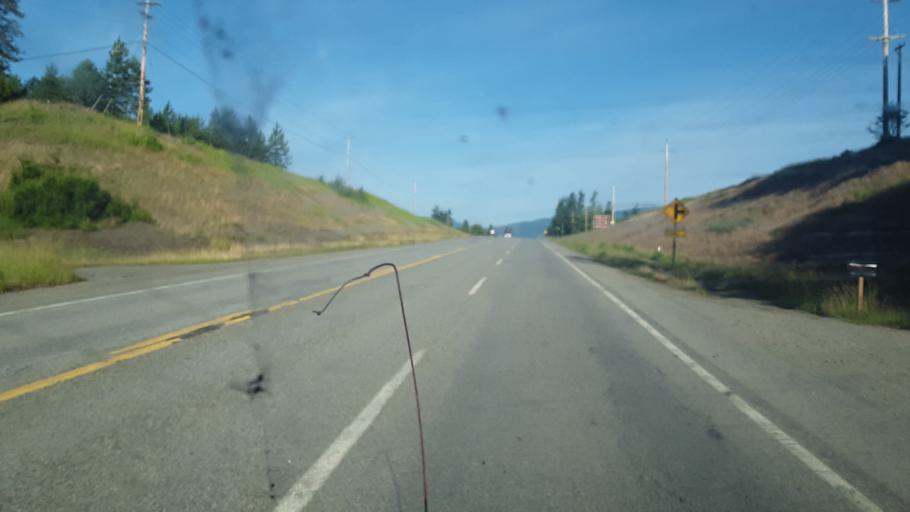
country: US
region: Idaho
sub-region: Boundary County
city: Bonners Ferry
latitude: 48.7317
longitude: -116.2532
